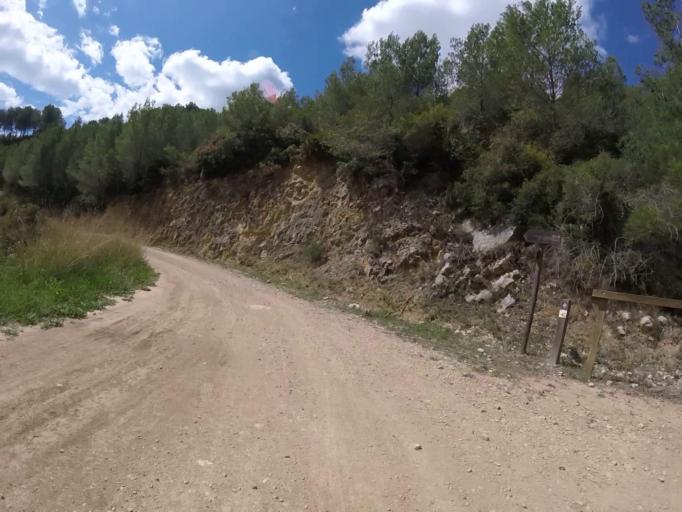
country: ES
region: Valencia
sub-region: Provincia de Castello
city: Santa Magdalena de Pulpis
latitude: 40.3110
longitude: 0.3178
